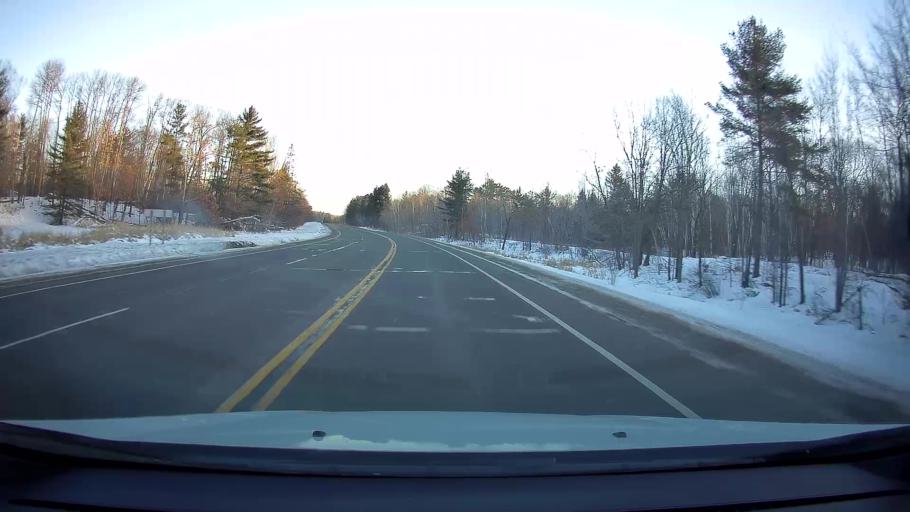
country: US
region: Wisconsin
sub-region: Barron County
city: Turtle Lake
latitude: 45.4542
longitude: -92.1032
